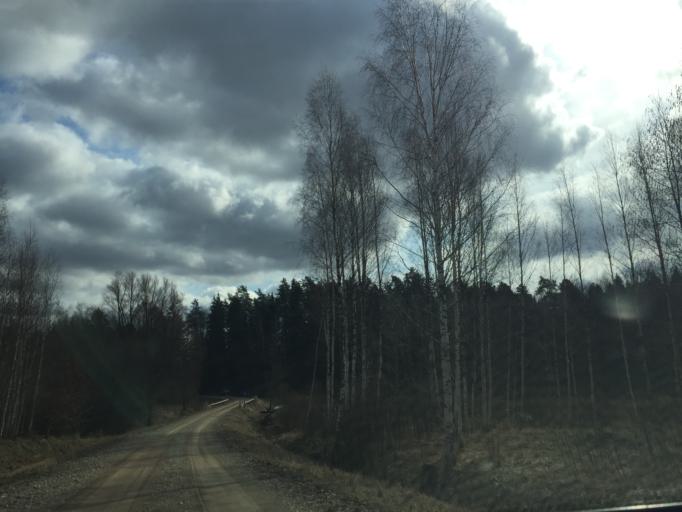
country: LV
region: Vecumnieki
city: Vecumnieki
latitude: 56.6006
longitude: 24.6270
